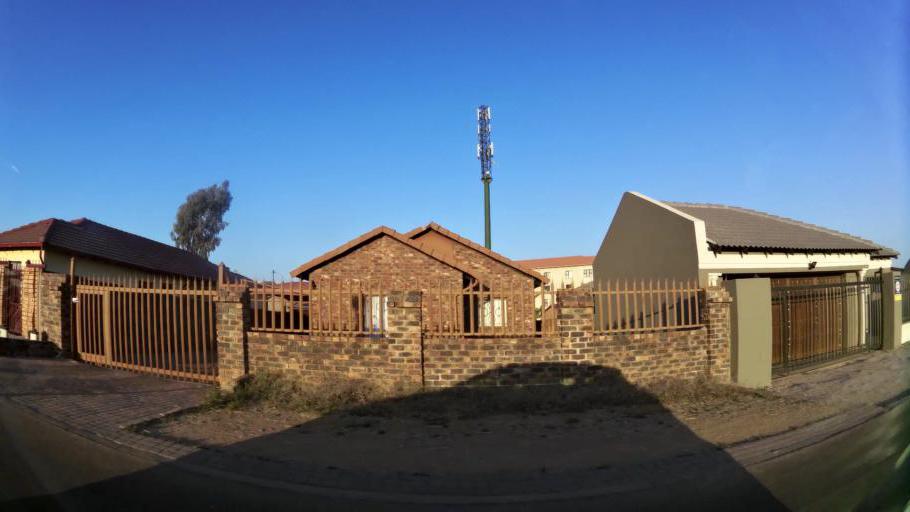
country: ZA
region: Gauteng
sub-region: City of Tshwane Metropolitan Municipality
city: Pretoria
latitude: -25.7467
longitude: 28.1107
